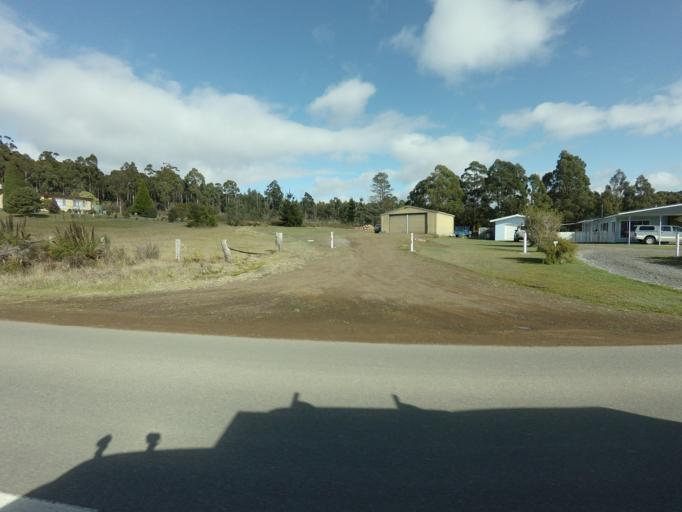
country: AU
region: Tasmania
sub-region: Huon Valley
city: Geeveston
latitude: -43.3388
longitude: 146.9715
